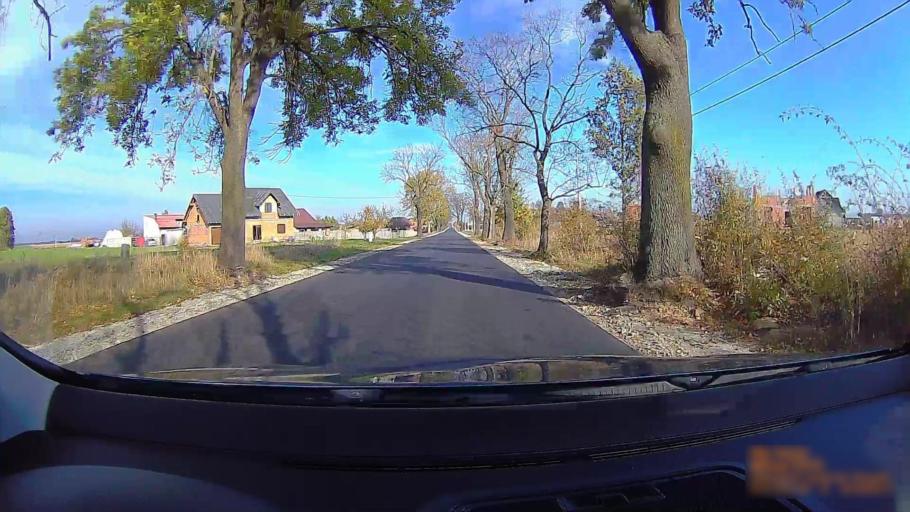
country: PL
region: Greater Poland Voivodeship
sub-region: Powiat ostrzeszowski
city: Doruchow
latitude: 51.4011
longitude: 18.0650
